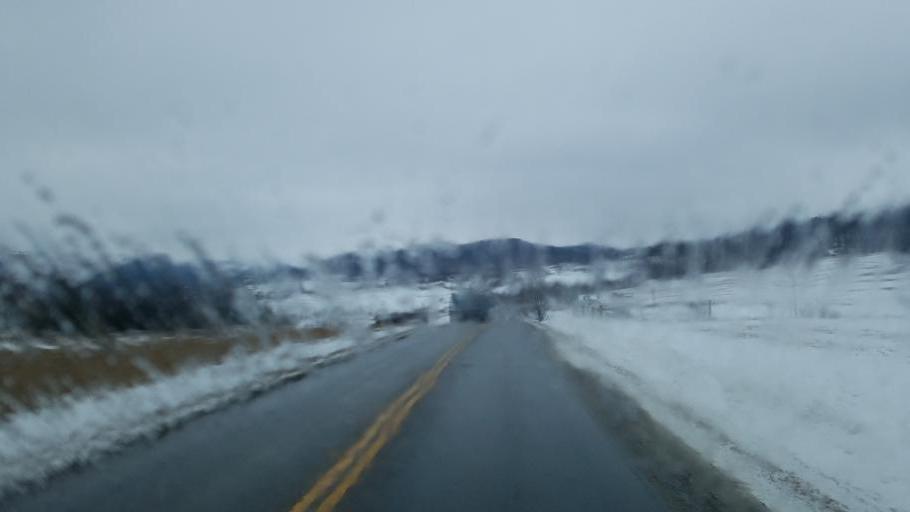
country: US
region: Pennsylvania
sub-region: Tioga County
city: Elkland
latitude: 42.0809
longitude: -77.4339
